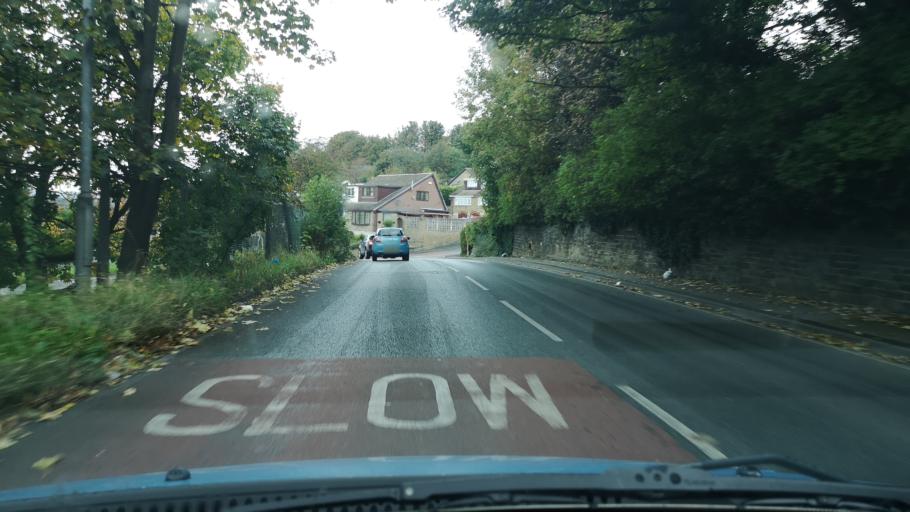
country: GB
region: England
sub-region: Kirklees
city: Heckmondwike
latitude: 53.7004
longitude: -1.6621
